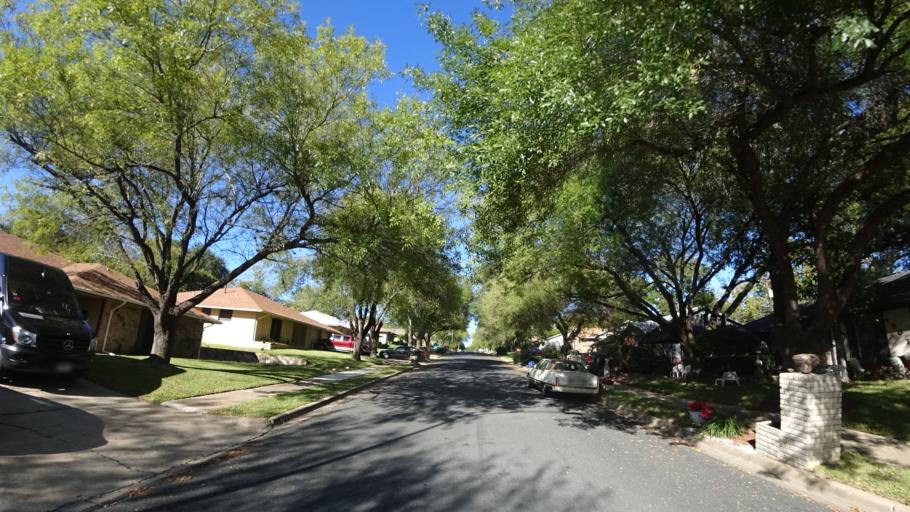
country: US
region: Texas
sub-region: Travis County
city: Austin
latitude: 30.2896
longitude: -97.6755
